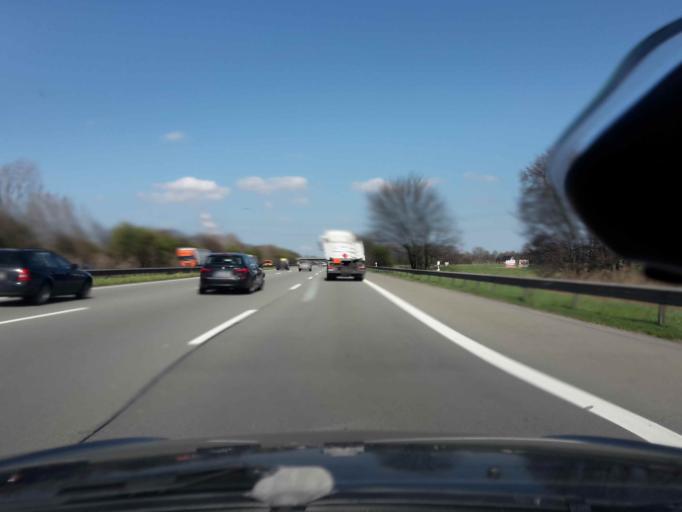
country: DE
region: Hamburg
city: Harburg
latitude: 53.4331
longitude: 10.0334
